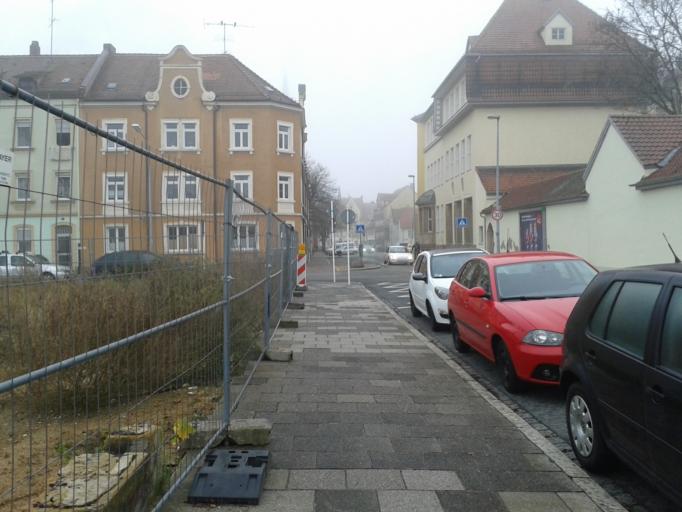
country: DE
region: Bavaria
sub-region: Upper Franconia
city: Bamberg
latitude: 49.8901
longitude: 10.9080
